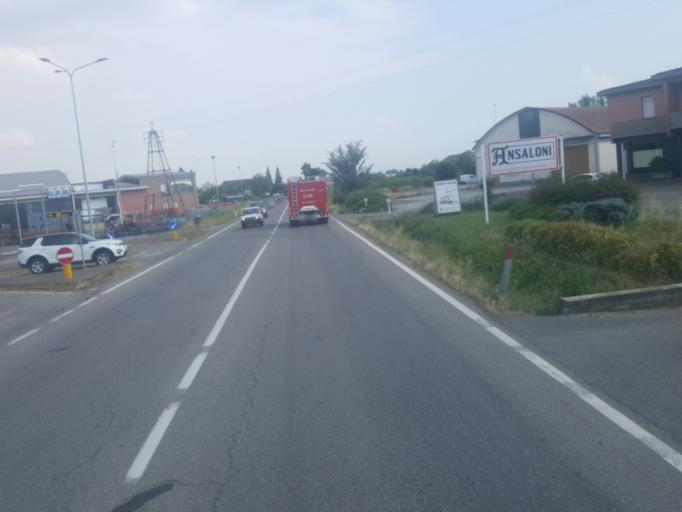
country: IT
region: Emilia-Romagna
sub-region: Provincia di Modena
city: Gaggio
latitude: 44.6167
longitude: 11.0132
